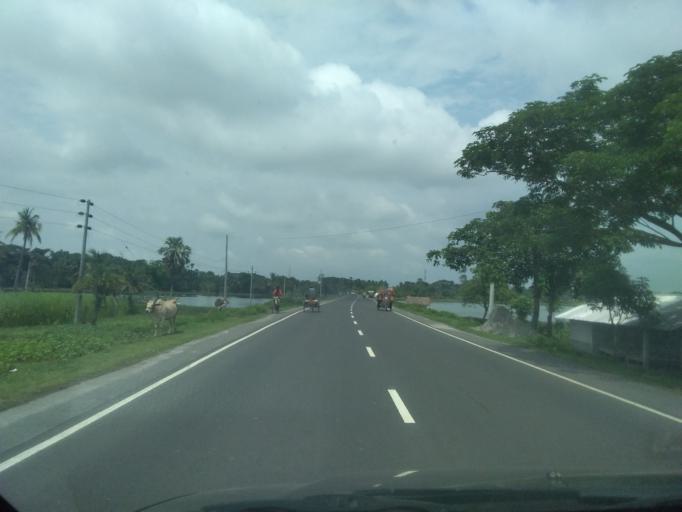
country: BD
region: Khulna
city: Kesabpur
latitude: 22.7838
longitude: 89.2103
